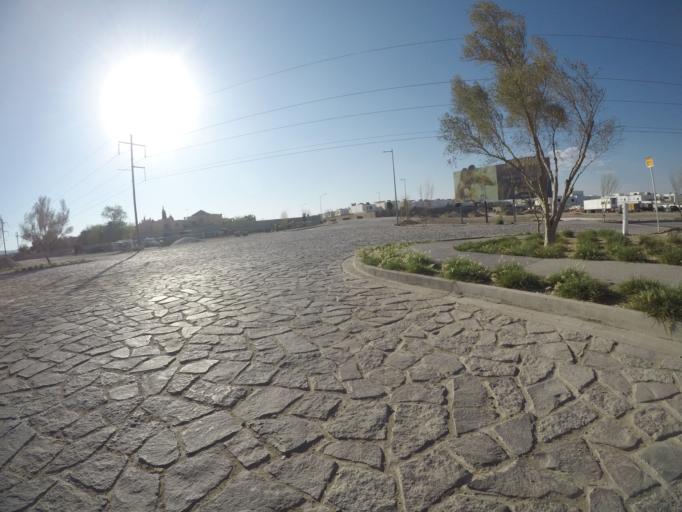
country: MX
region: Chihuahua
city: Ciudad Juarez
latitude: 31.7025
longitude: -106.3918
